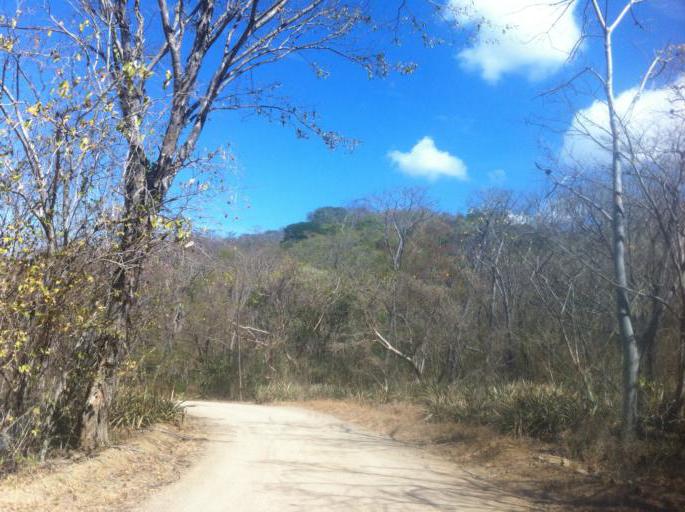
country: NI
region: Rivas
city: Tola
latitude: 11.3806
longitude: -86.0265
